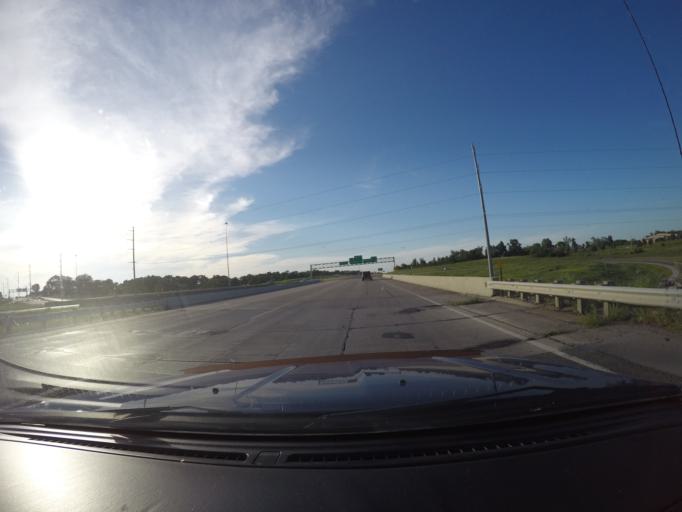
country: US
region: Kansas
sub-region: Wyandotte County
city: Edwardsville
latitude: 39.1281
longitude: -94.8161
